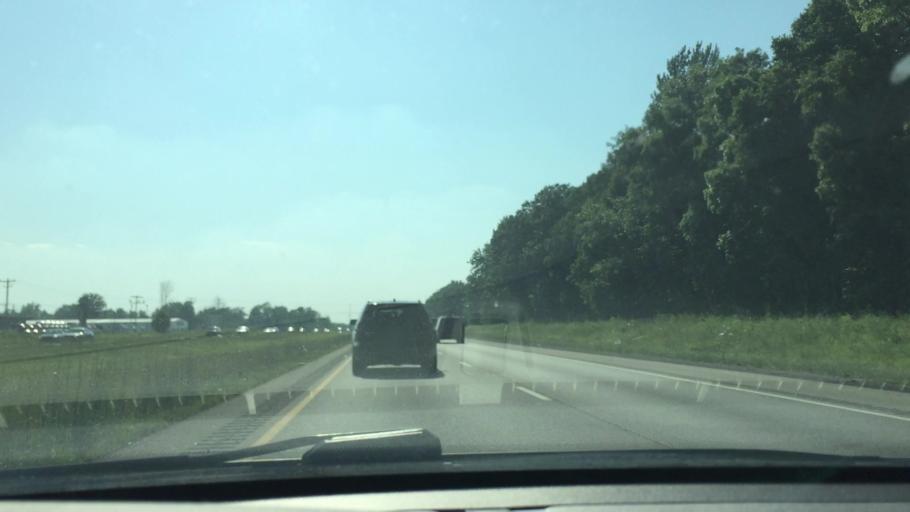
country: US
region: Ohio
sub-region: Licking County
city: Etna
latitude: 39.9493
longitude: -82.6920
